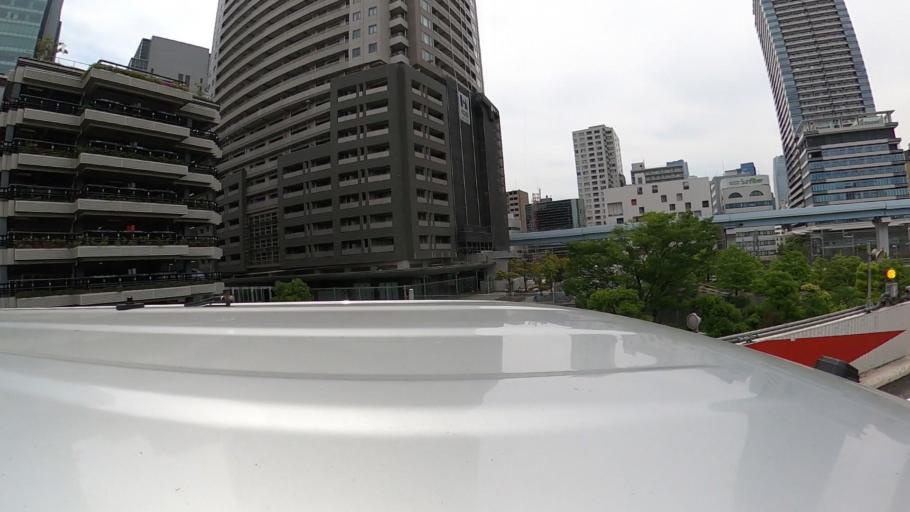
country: JP
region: Tokyo
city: Tokyo
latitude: 35.6585
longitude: 139.7598
